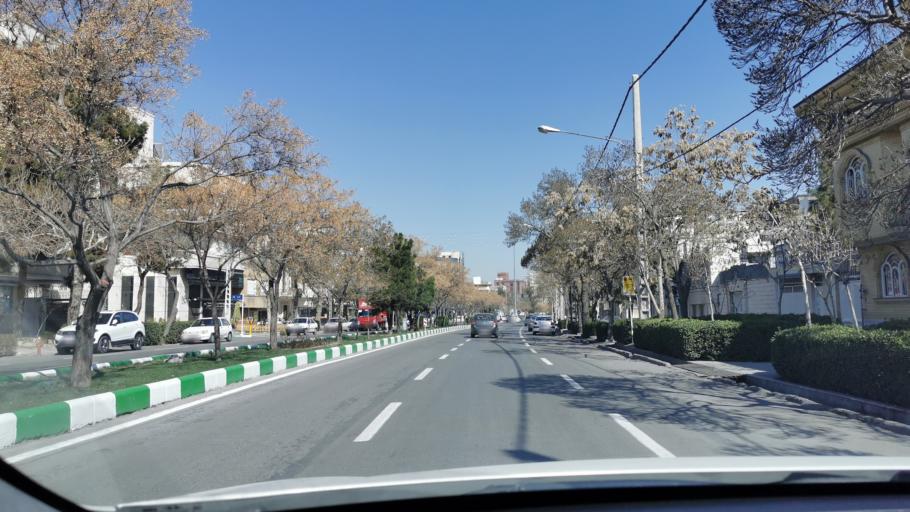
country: IR
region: Razavi Khorasan
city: Mashhad
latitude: 36.2908
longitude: 59.5723
